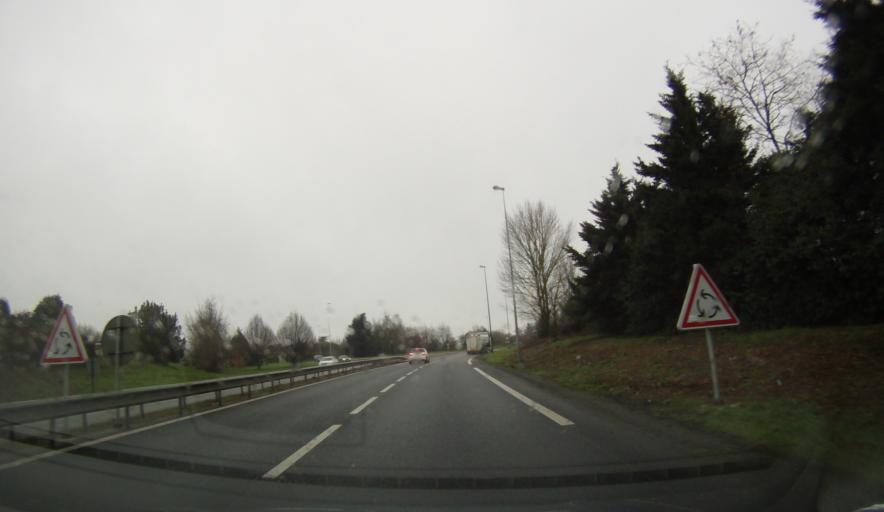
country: FR
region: Brittany
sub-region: Departement d'Ille-et-Vilaine
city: Vern-sur-Seiche
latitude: 48.0507
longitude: -1.6089
